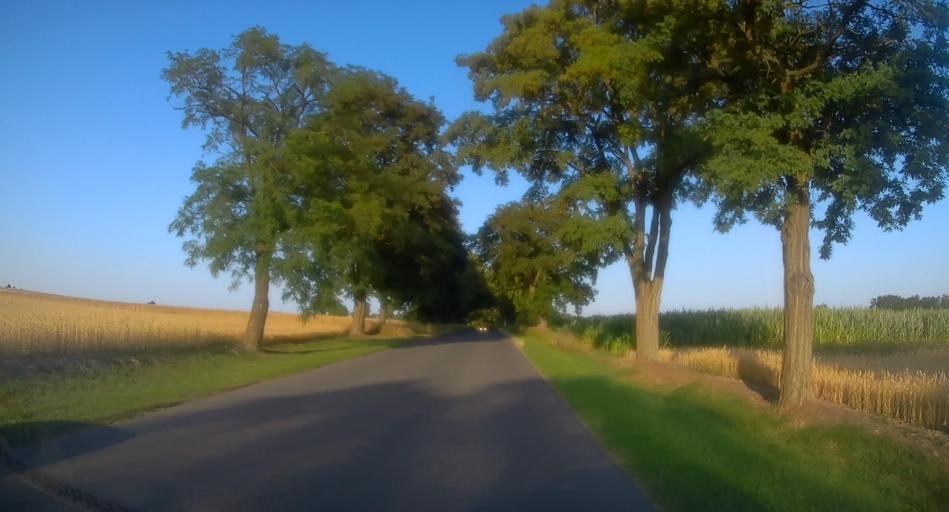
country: PL
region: Lodz Voivodeship
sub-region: Powiat skierniewicki
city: Kaweczyn Nowy
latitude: 51.8838
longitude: 20.2619
